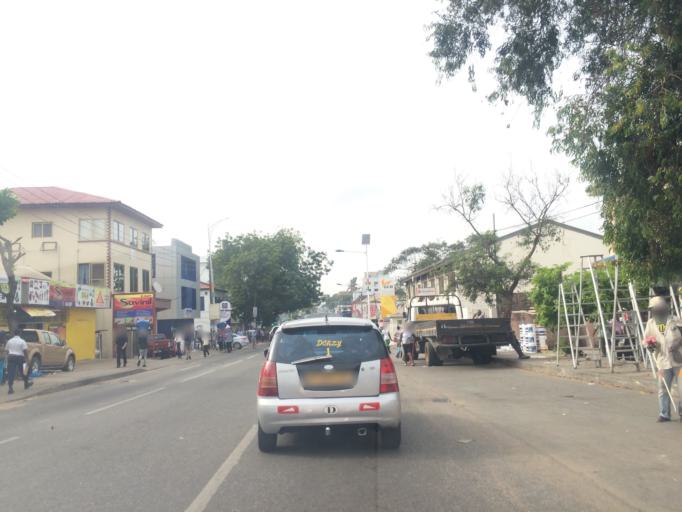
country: GH
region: Greater Accra
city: Accra
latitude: 5.5547
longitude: -0.2087
